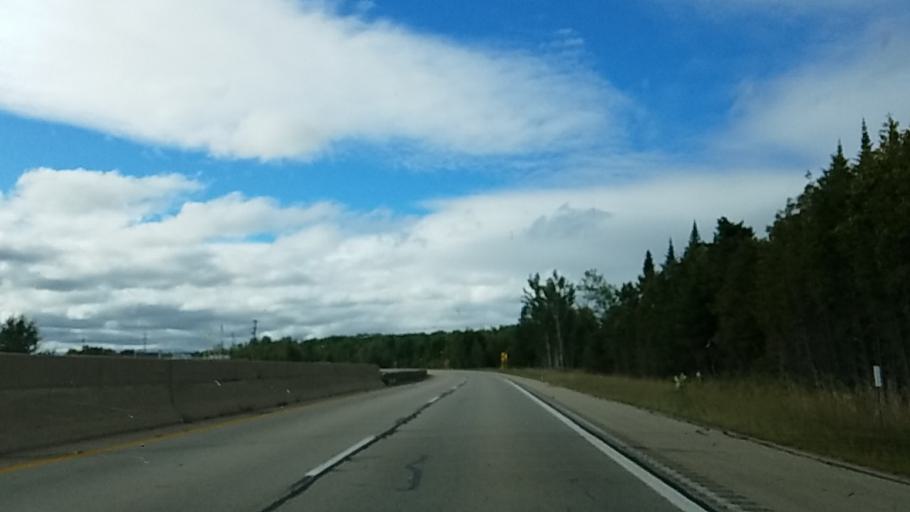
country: US
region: Michigan
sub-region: Mackinac County
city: Saint Ignace
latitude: 45.7687
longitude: -84.7352
